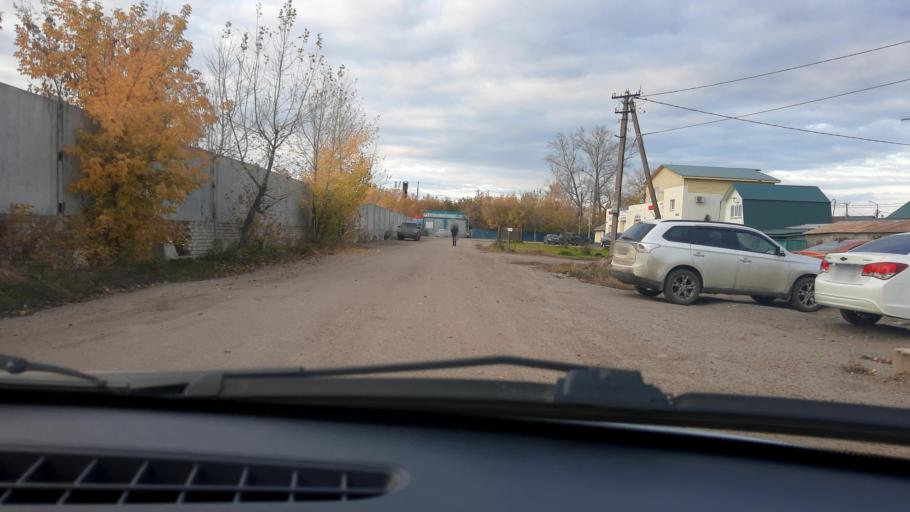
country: RU
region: Bashkortostan
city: Ufa
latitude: 54.7482
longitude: 55.9131
